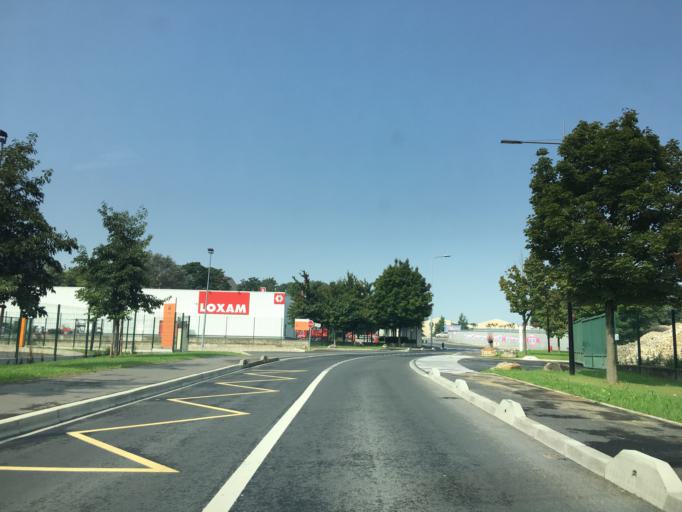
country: FR
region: Ile-de-France
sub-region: Departement du Val-de-Marne
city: Bonneuil-sur-Marne
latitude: 48.7756
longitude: 2.4921
